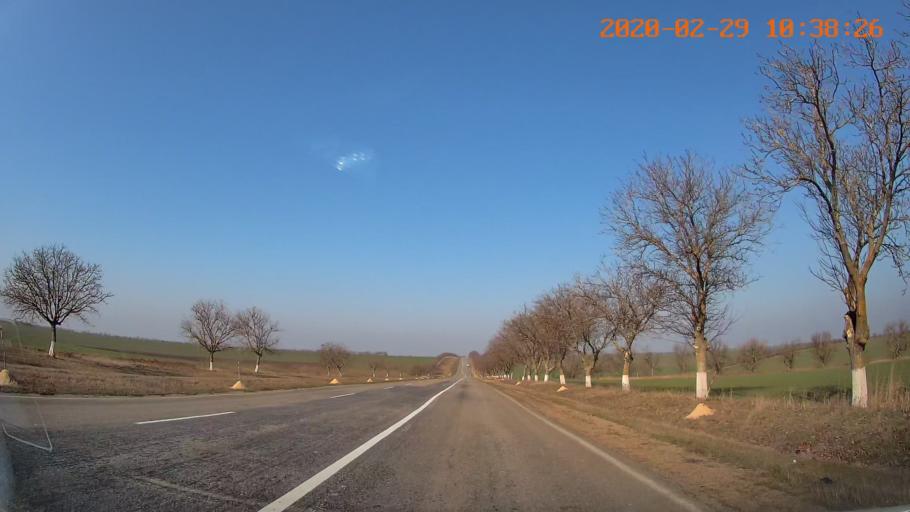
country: MD
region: Anenii Noi
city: Varnita
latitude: 47.0160
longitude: 29.4731
